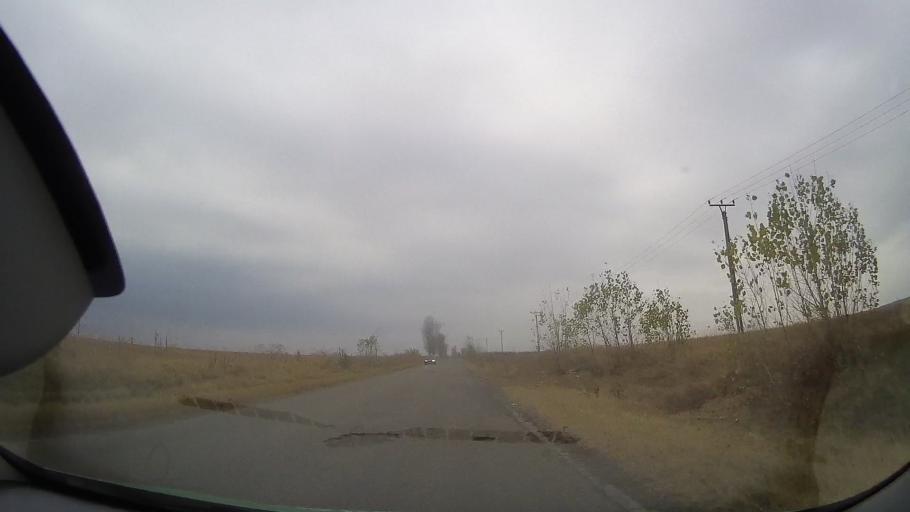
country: RO
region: Buzau
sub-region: Comuna Pogoanele
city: Pogoanele
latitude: 44.8869
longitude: 26.9575
